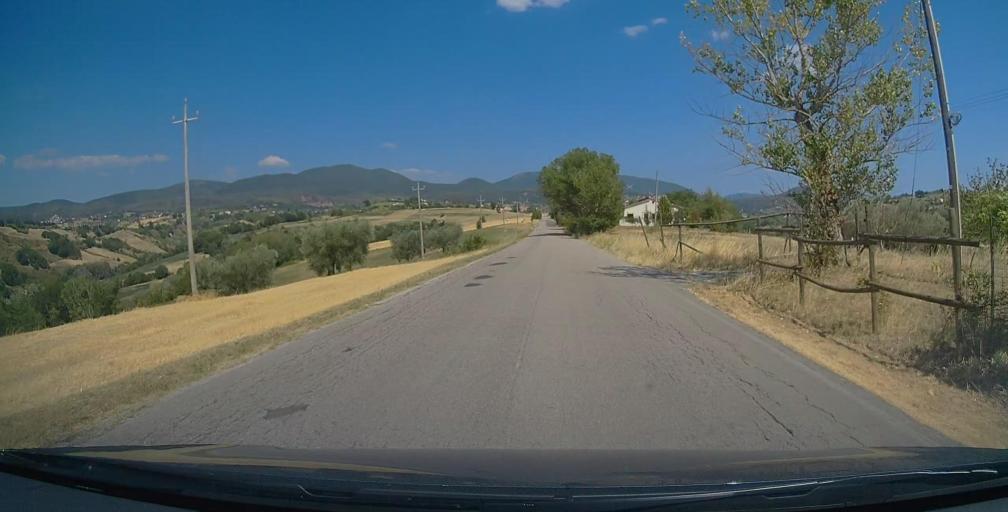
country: IT
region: Umbria
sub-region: Provincia di Terni
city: Otricoli
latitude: 42.4066
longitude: 12.5127
